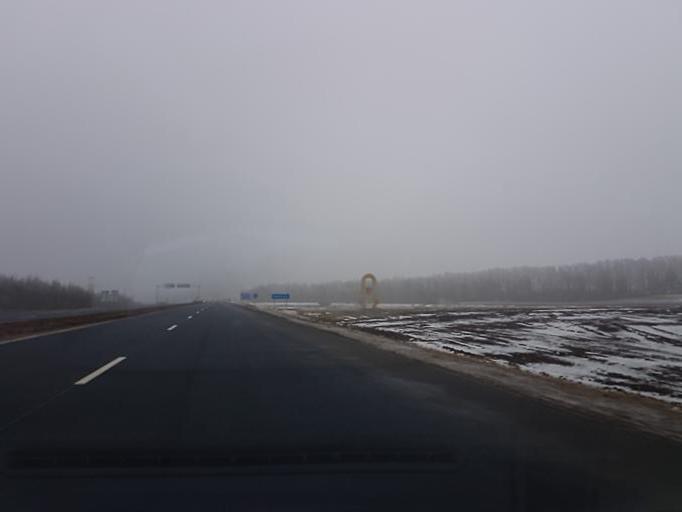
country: BY
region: Minsk
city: Samakhvalavichy
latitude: 53.7058
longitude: 27.4463
